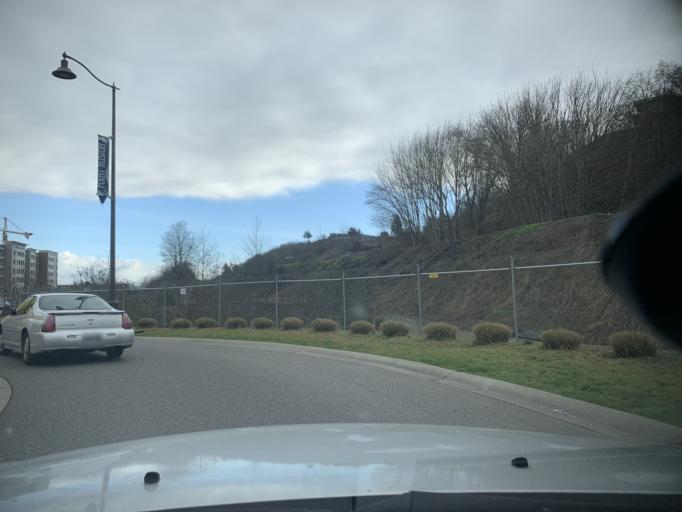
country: US
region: Washington
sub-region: Pierce County
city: Fircrest
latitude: 47.2976
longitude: -122.5056
